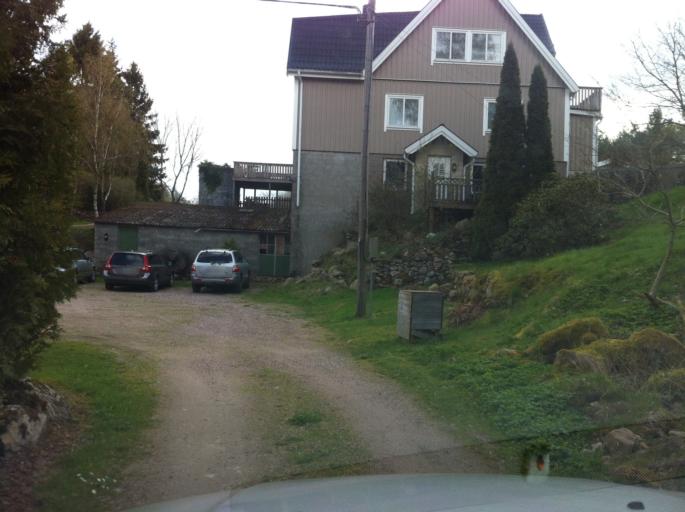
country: SE
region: Skane
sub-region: Hoors Kommun
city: Satofta
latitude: 55.9120
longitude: 13.6126
